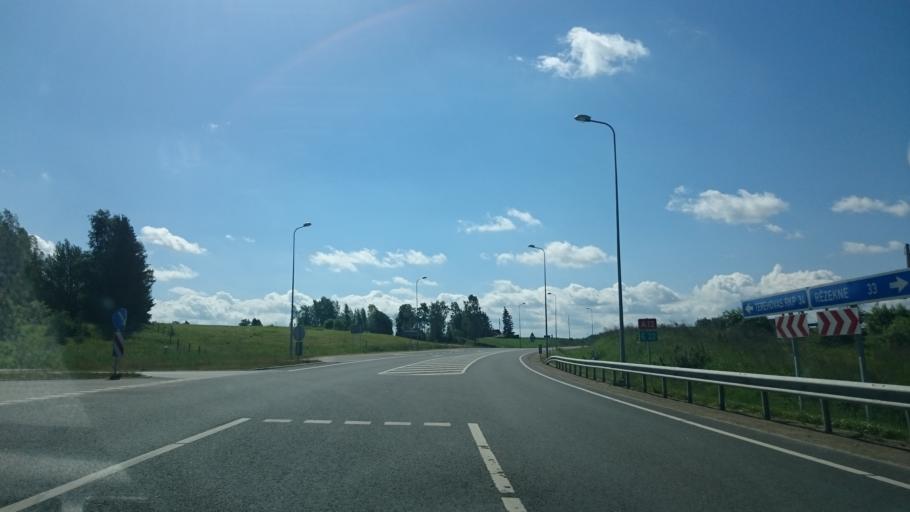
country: LV
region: Ludzas Rajons
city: Ludza
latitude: 56.5148
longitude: 27.7532
